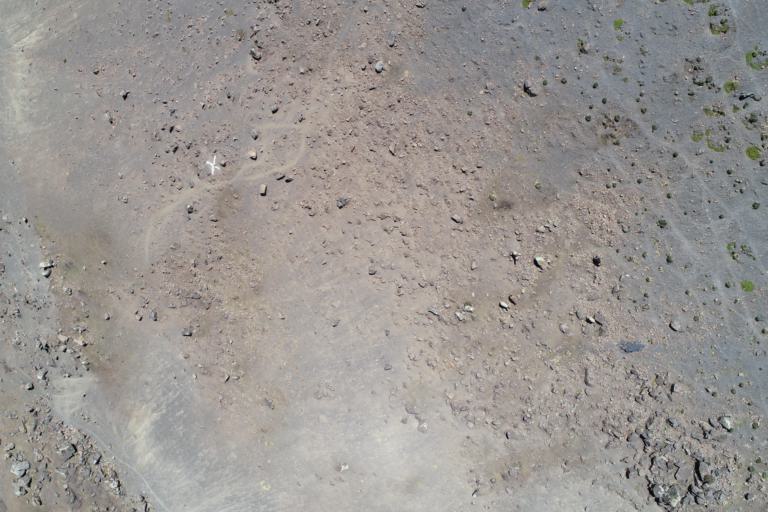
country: BO
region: La Paz
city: La Paz
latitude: -16.6219
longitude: -67.8269
